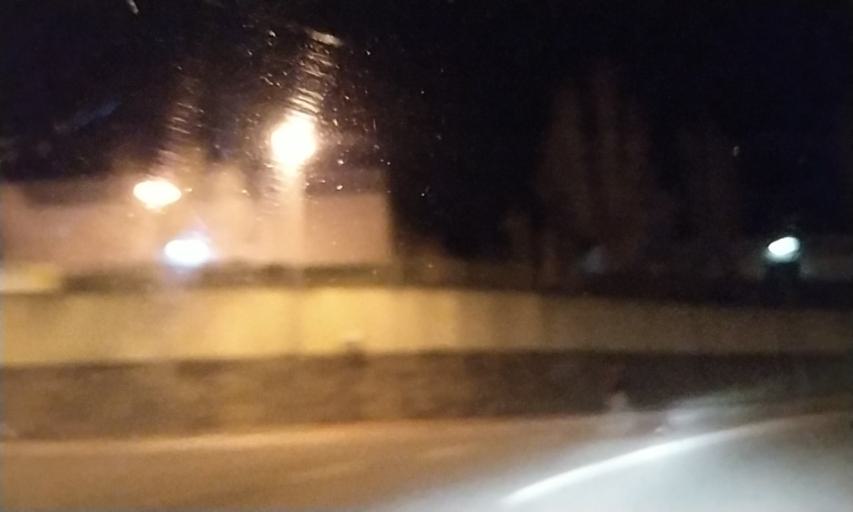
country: PT
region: Castelo Branco
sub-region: Concelho do Fundao
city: Fundao
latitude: 40.1338
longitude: -7.5062
